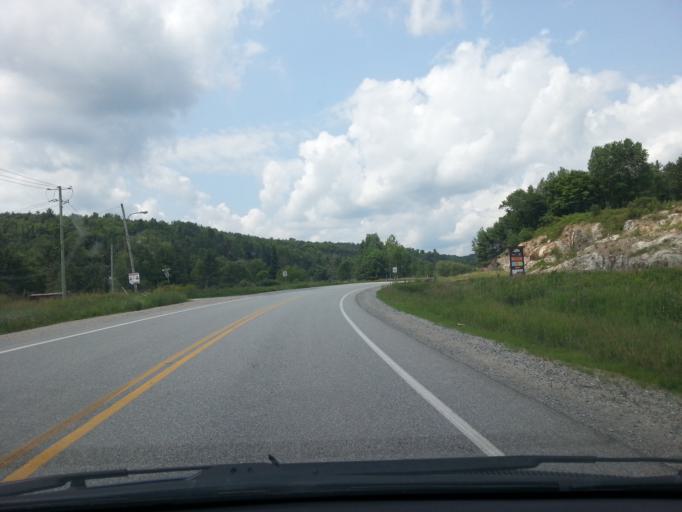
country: CA
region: Quebec
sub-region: Outaouais
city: Val-des-Monts
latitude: 45.6523
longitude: -75.6858
